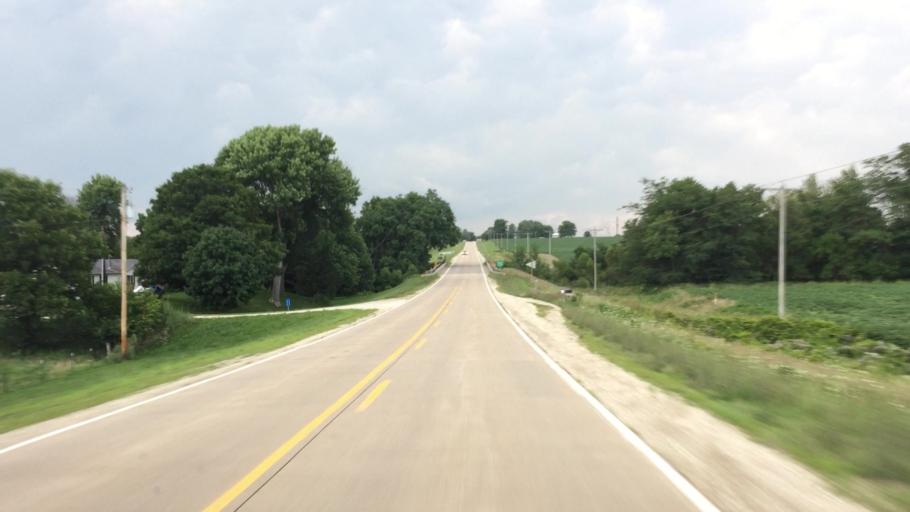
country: US
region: Iowa
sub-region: Lee County
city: Fort Madison
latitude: 40.7223
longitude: -91.3298
